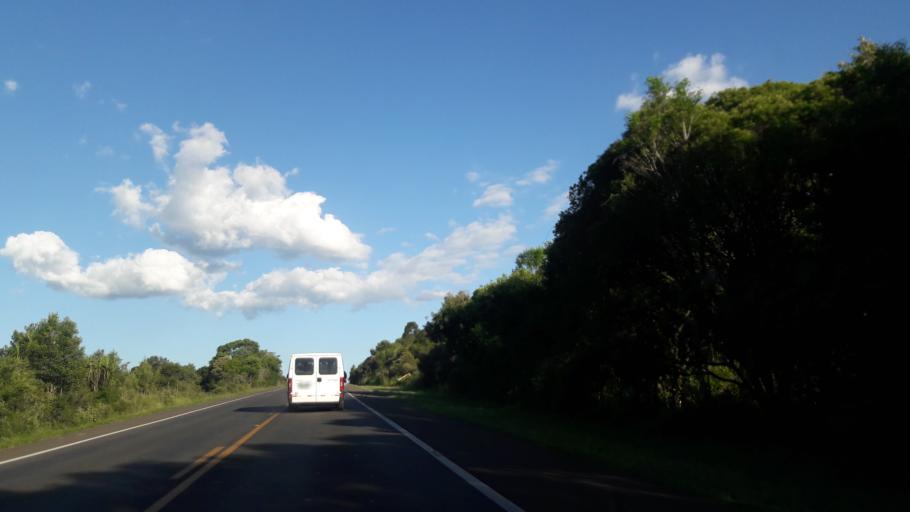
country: BR
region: Parana
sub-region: Guarapuava
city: Guarapuava
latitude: -25.3685
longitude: -51.3312
